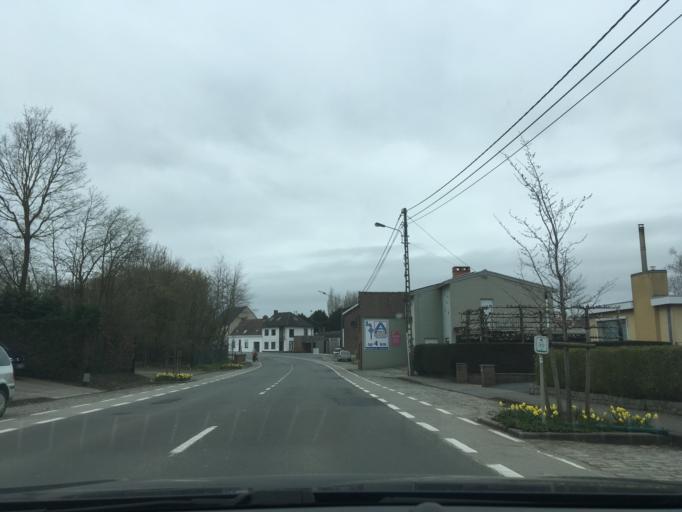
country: BE
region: Flanders
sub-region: Provincie West-Vlaanderen
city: Kortemark
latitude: 51.0278
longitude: 3.0587
